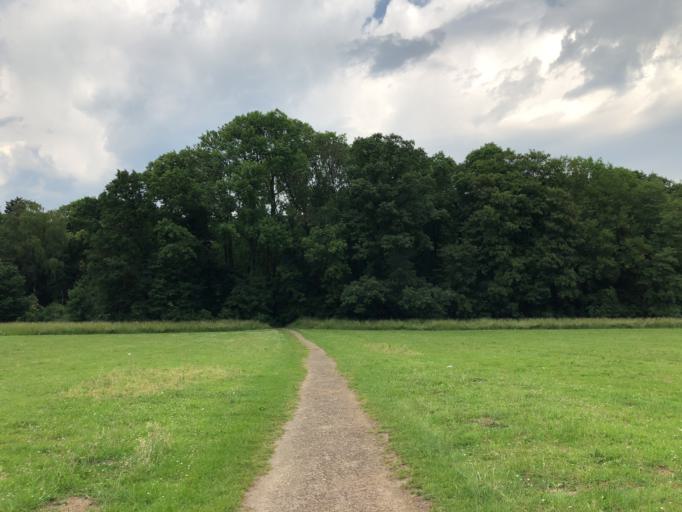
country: DE
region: North Rhine-Westphalia
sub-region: Regierungsbezirk Dusseldorf
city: Erkrath
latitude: 51.1925
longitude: 6.8521
